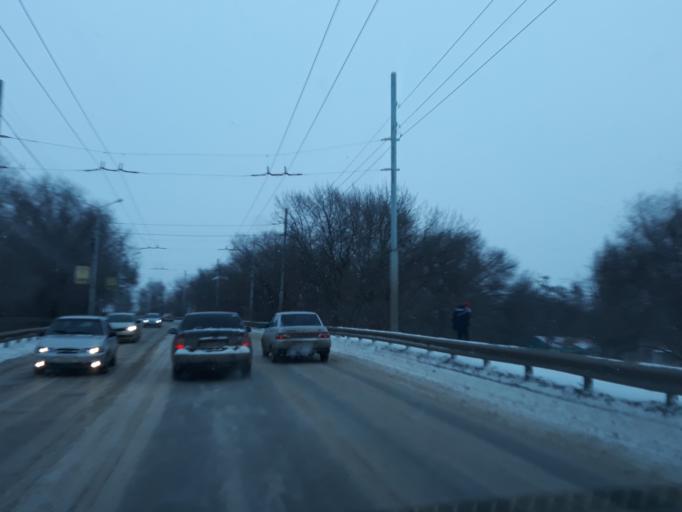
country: RU
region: Rostov
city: Taganrog
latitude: 47.2634
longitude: 38.9261
